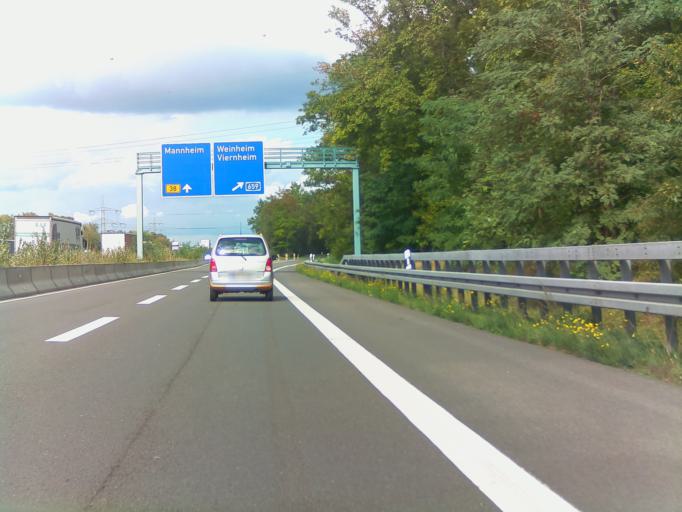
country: DE
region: Hesse
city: Viernheim
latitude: 49.5180
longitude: 8.5605
